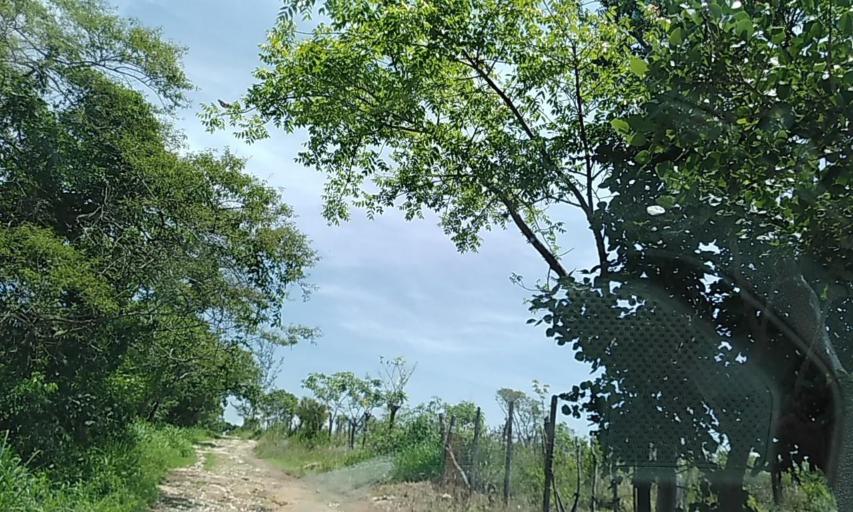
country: MX
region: Veracruz
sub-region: Emiliano Zapata
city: Dos Rios
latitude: 19.4409
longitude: -96.7588
